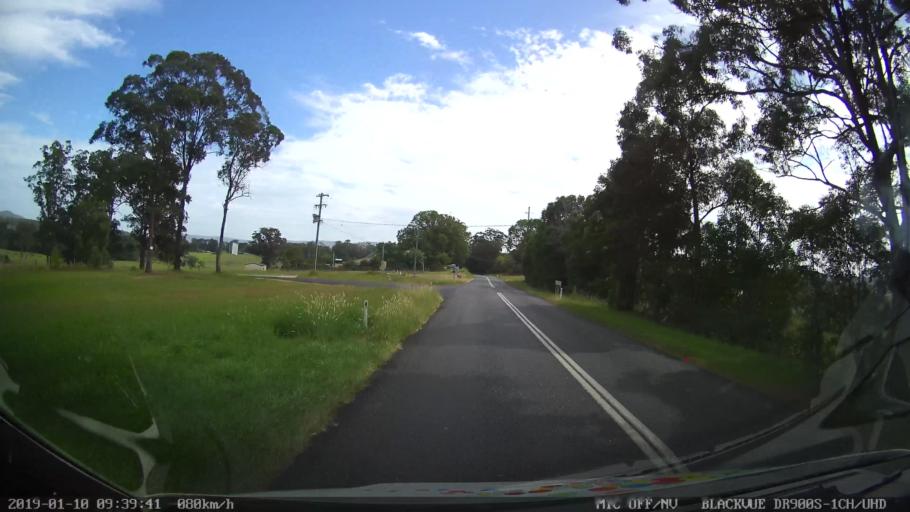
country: AU
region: New South Wales
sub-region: Coffs Harbour
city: Nana Glen
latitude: -30.1607
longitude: 153.0037
